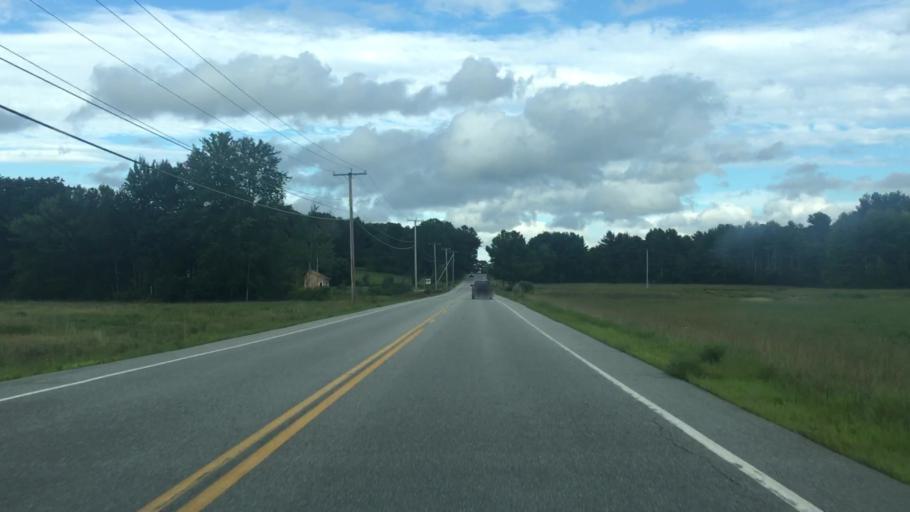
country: US
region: Maine
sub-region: York County
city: Dayton
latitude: 43.5447
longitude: -70.5367
